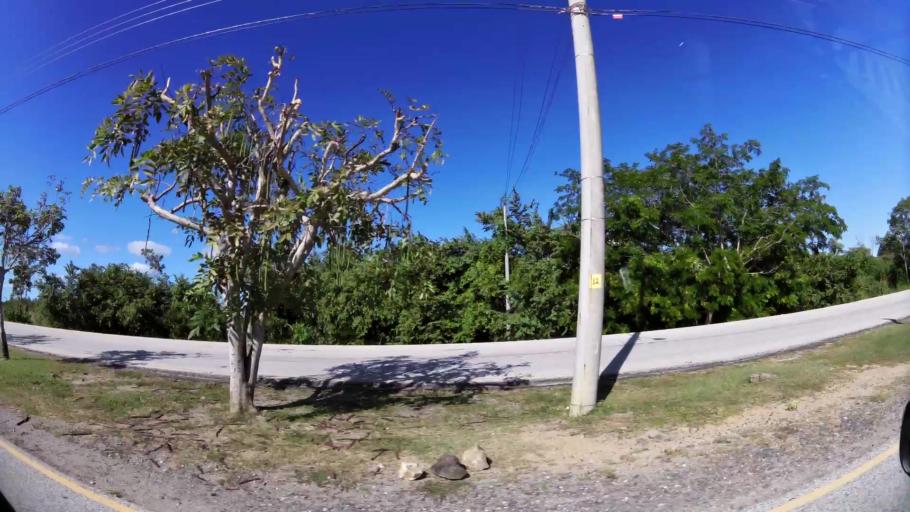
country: CR
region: Guanacaste
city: Liberia
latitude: 10.6023
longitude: -85.5310
